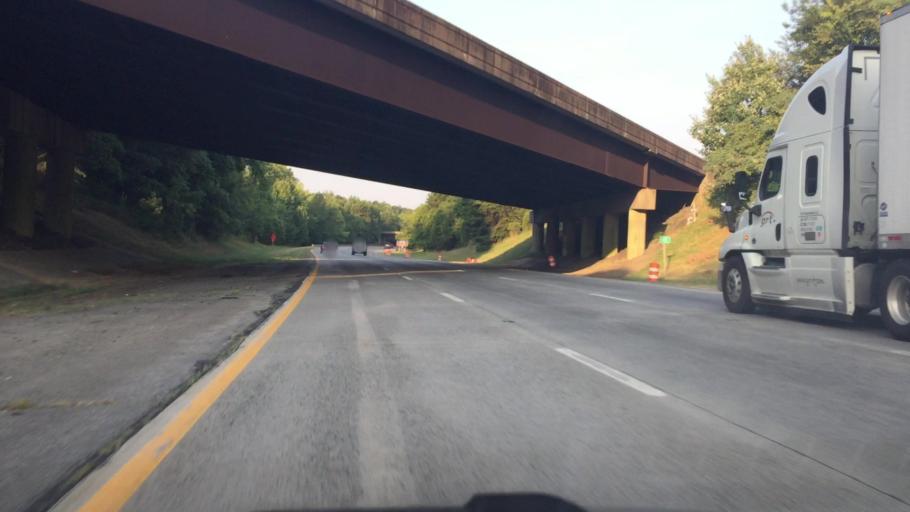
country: US
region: North Carolina
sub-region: Davidson County
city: Thomasville
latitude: 35.8497
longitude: -80.1186
